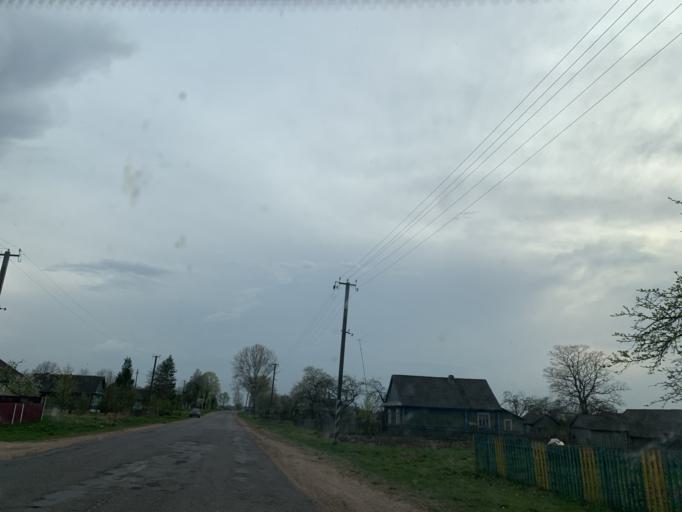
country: BY
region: Minsk
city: Kapyl'
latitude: 53.2759
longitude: 26.9704
